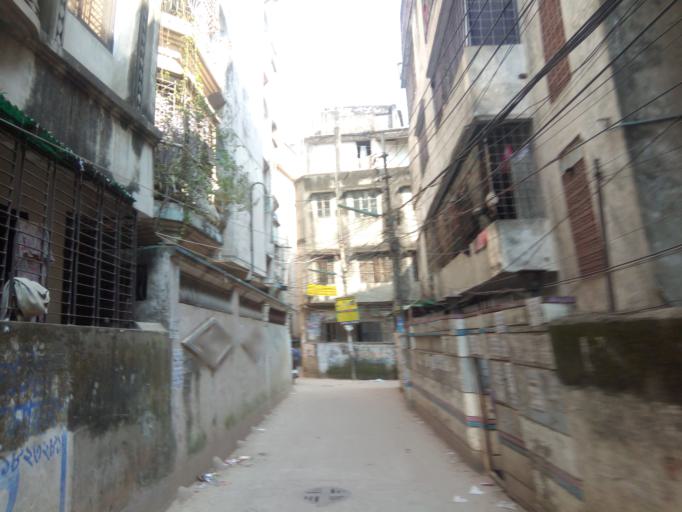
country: BD
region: Dhaka
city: Paltan
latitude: 23.7543
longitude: 90.4136
